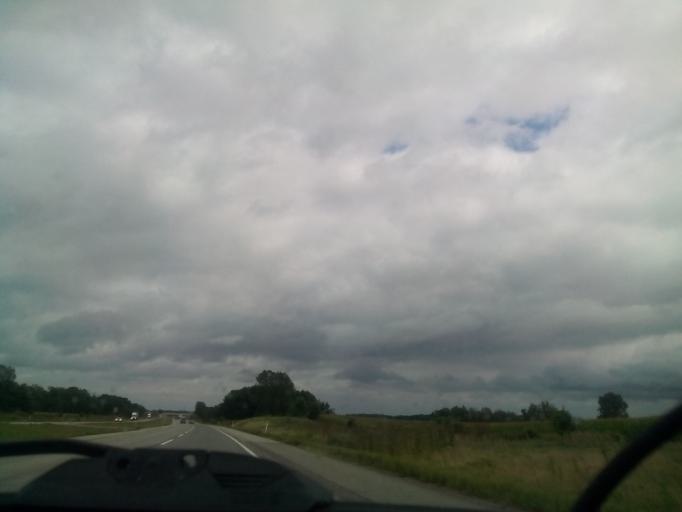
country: US
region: Indiana
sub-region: Steuben County
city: Fremont
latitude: 41.6934
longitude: -84.9057
